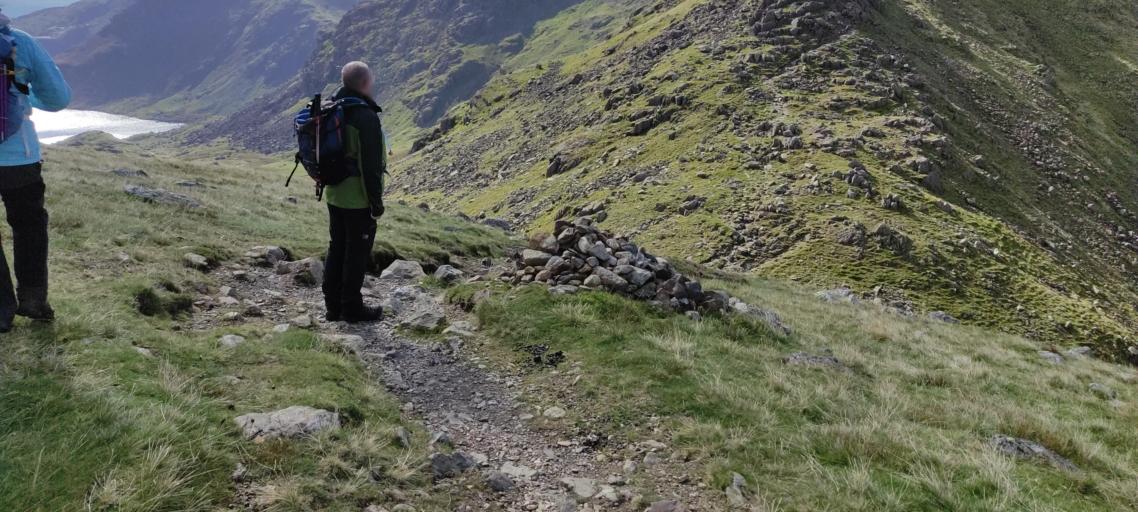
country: GB
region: England
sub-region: Cumbria
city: Ambleside
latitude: 54.3979
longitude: -3.1121
